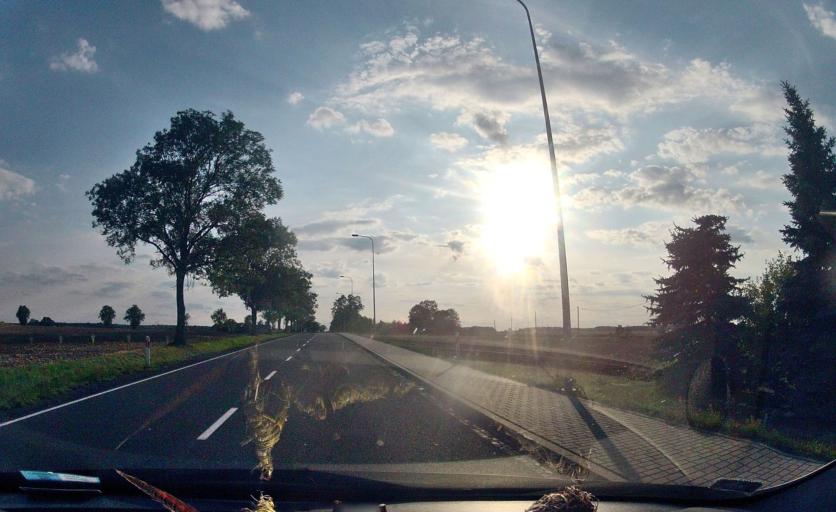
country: PL
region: Opole Voivodeship
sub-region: Powiat oleski
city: Gorzow Slaski
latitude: 51.0115
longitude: 18.3730
